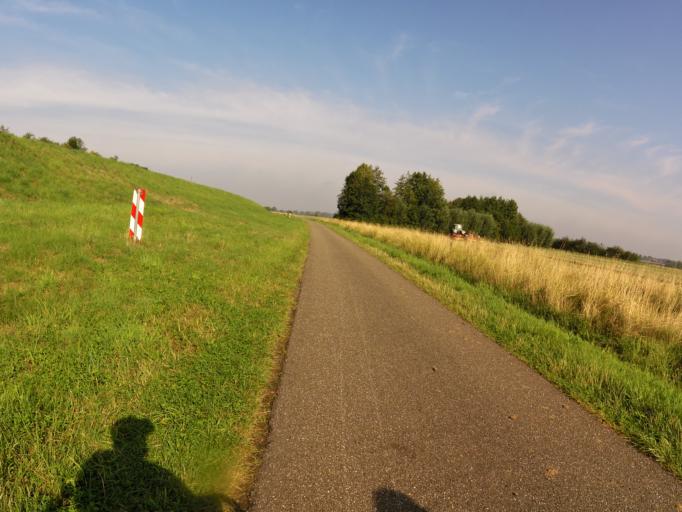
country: DE
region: Lower Saxony
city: Langwedel
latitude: 52.9615
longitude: 9.1751
